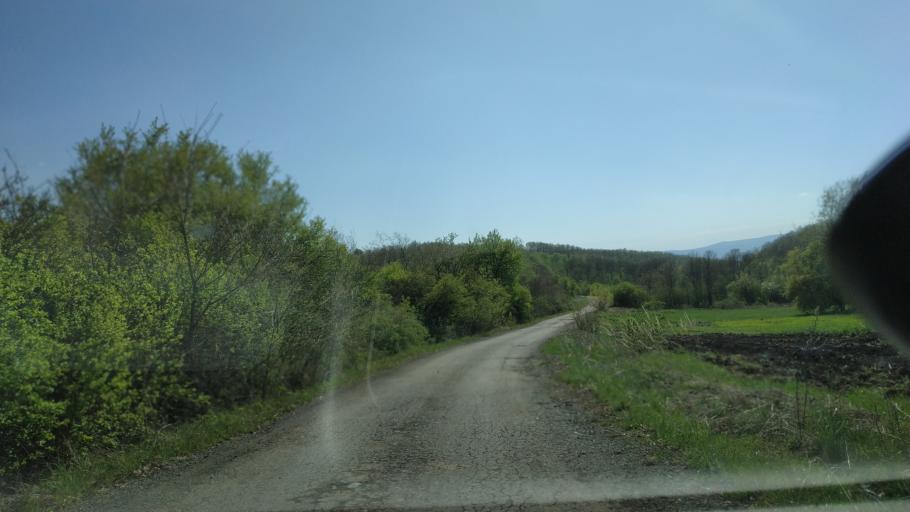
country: RS
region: Central Serbia
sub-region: Zajecarski Okrug
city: Soko Banja
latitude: 43.5107
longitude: 21.9026
